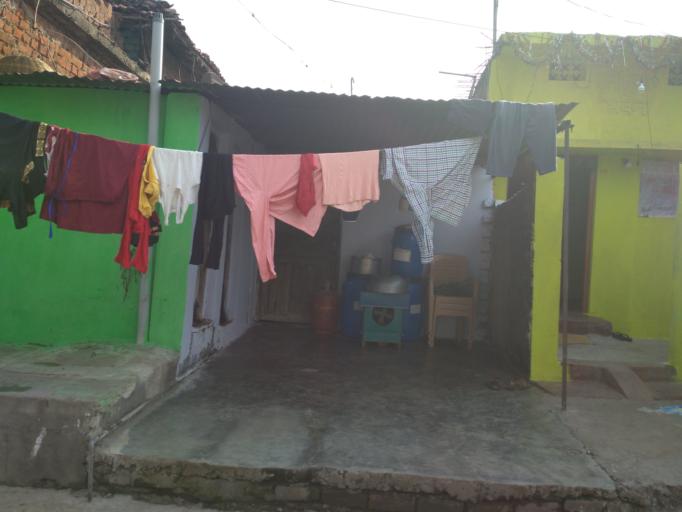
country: IN
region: Maharashtra
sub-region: Nagpur Division
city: Mohpa
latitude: 21.3093
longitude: 78.8275
